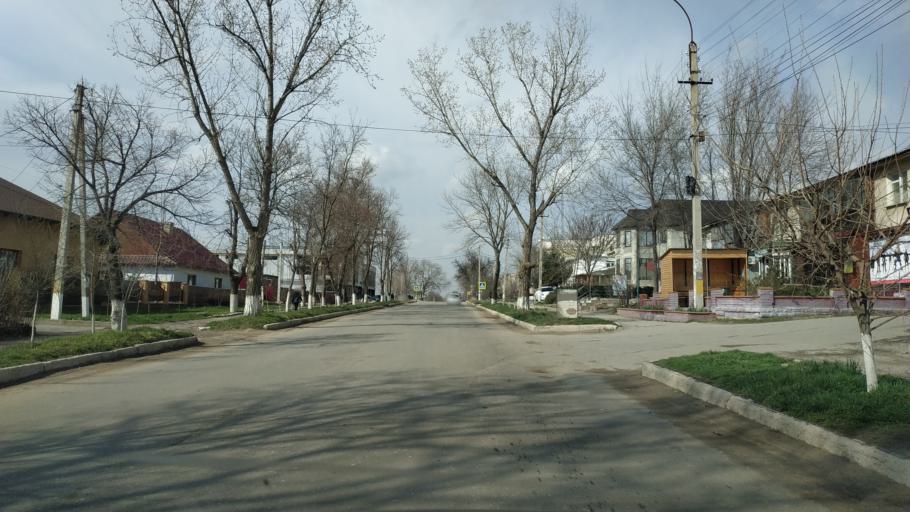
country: MD
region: Gagauzia
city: Vulcanesti
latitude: 45.6860
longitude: 28.4047
